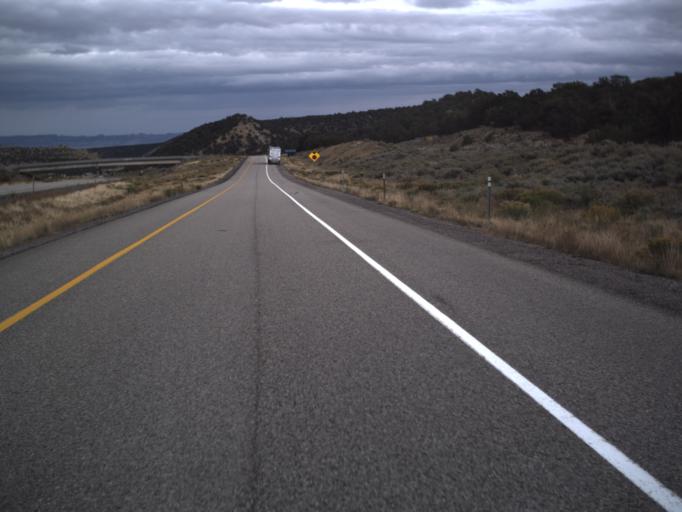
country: US
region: Utah
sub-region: Wayne County
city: Loa
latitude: 38.7568
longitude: -111.4323
